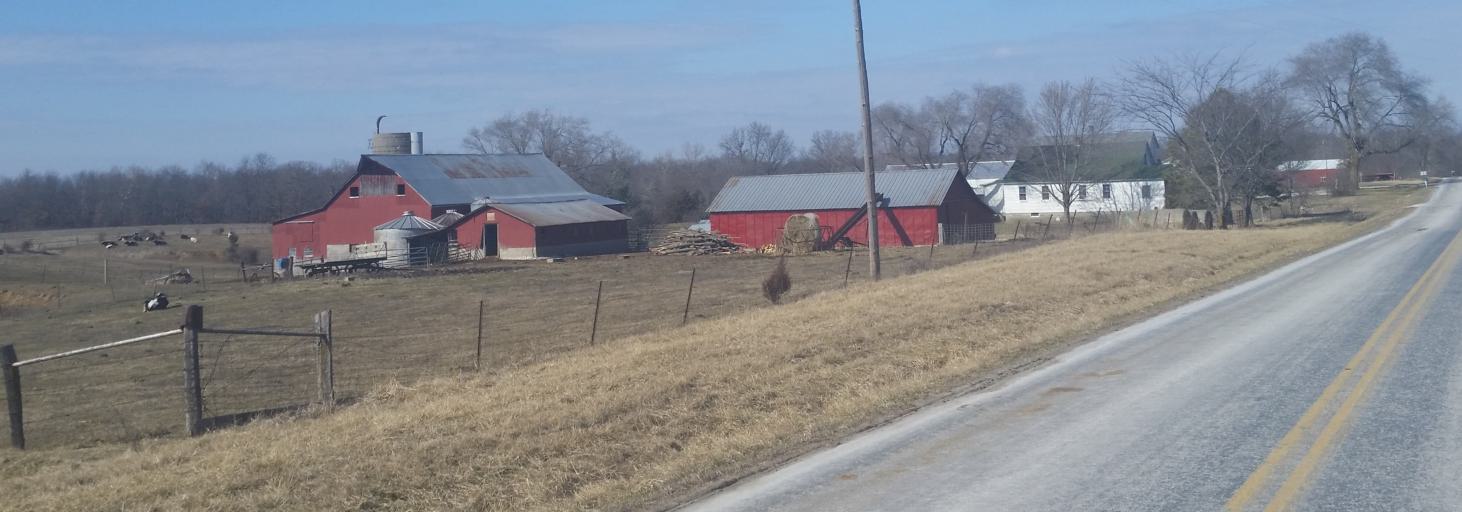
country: US
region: Missouri
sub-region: Boone County
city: Centralia
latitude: 39.3332
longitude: -92.2694
